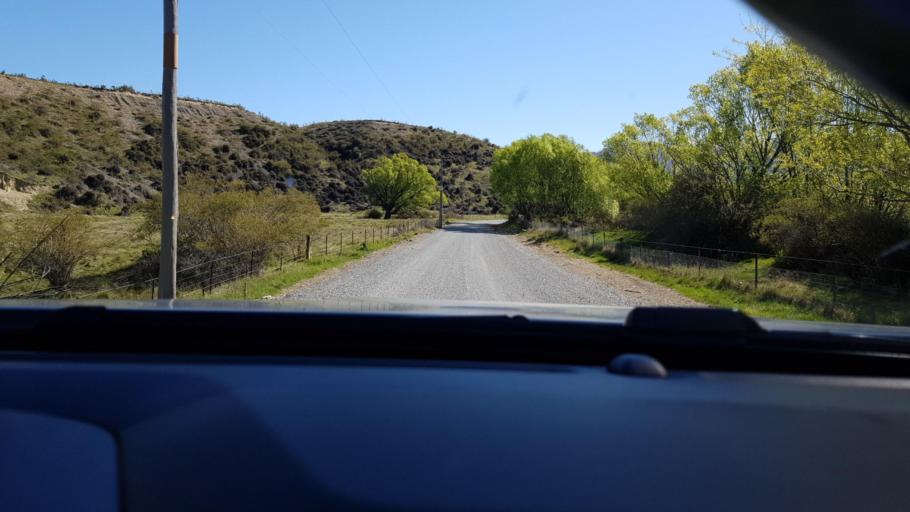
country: NZ
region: Otago
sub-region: Queenstown-Lakes District
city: Wanaka
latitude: -44.4628
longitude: 169.8921
